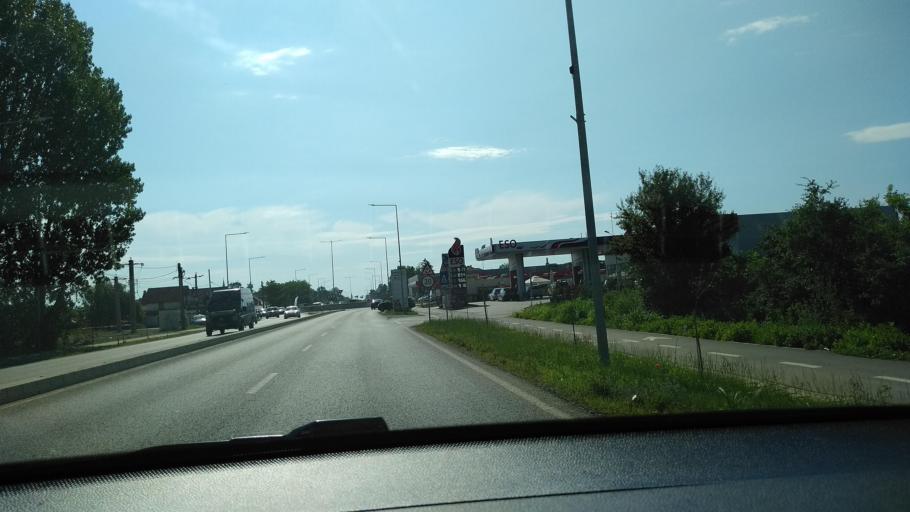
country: RO
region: Timis
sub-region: Comuna Mosnita Noua
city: Mosnita Noua
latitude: 45.7205
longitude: 21.3135
